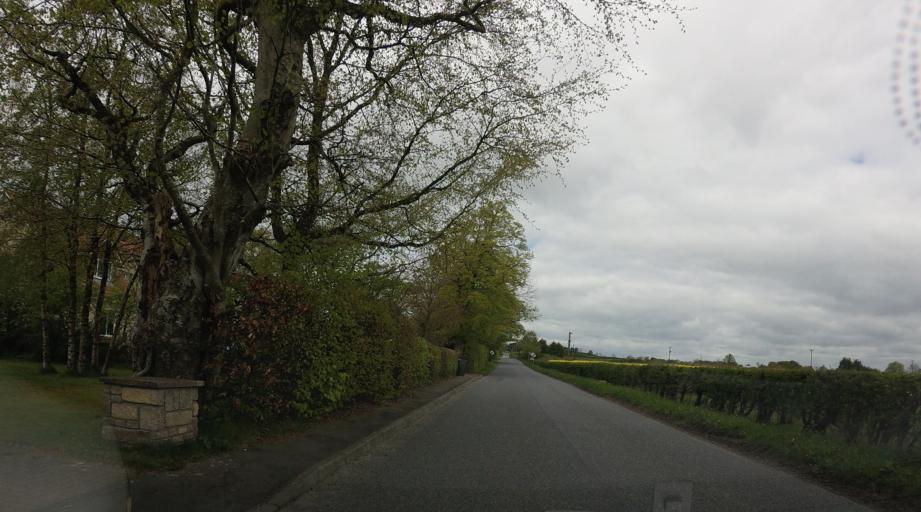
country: GB
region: Scotland
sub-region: Perth and Kinross
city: Milnathort
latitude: 56.2431
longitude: -3.3736
